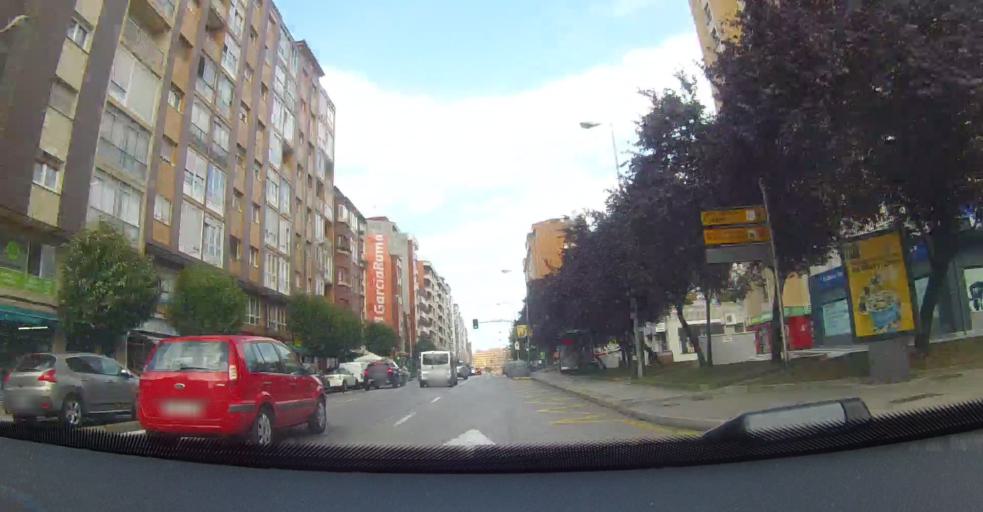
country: ES
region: Asturias
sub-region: Province of Asturias
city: Gijon
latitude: 43.5355
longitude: -5.6531
